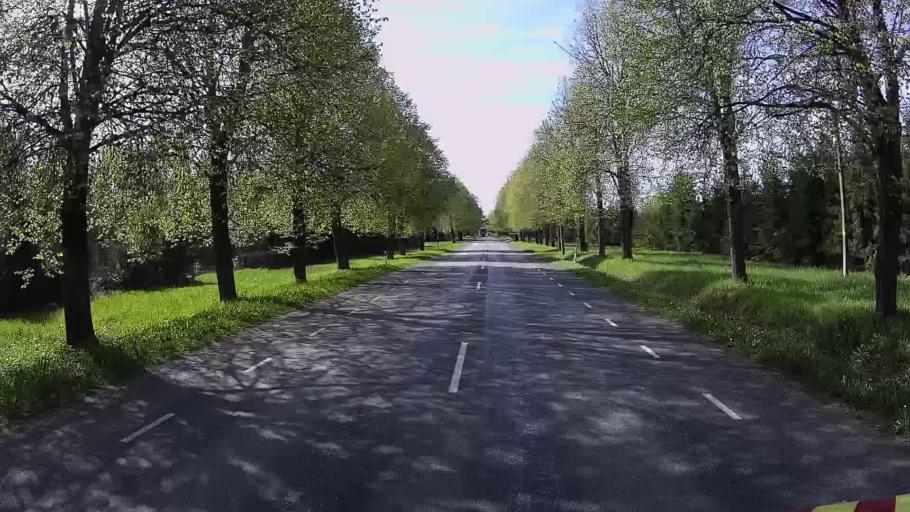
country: EE
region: Polvamaa
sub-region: Polva linn
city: Polva
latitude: 58.2031
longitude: 27.0760
